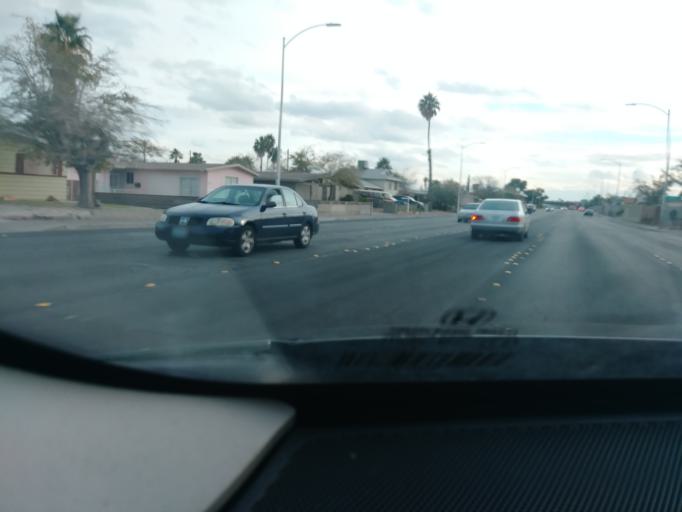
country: US
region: Nevada
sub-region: Clark County
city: Spring Valley
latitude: 36.1796
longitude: -115.2239
